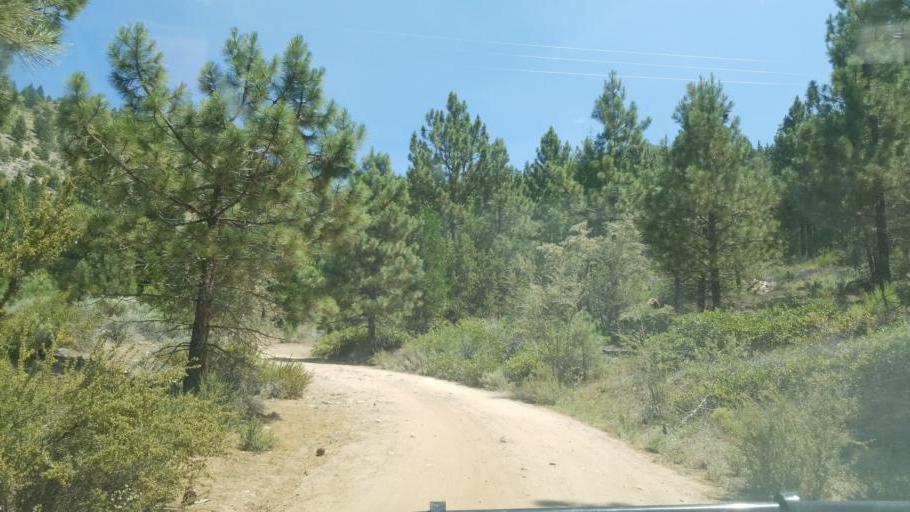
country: US
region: California
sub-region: Lassen County
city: Susanville
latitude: 40.5640
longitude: -120.7572
